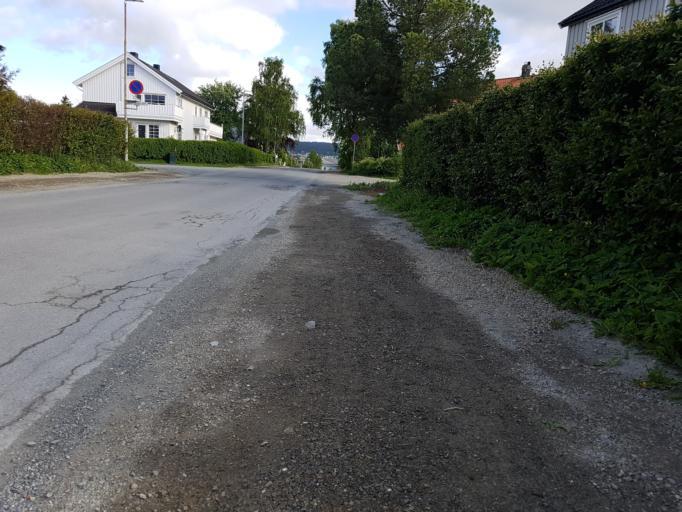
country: NO
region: Sor-Trondelag
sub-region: Trondheim
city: Trondheim
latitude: 63.4337
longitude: 10.4403
